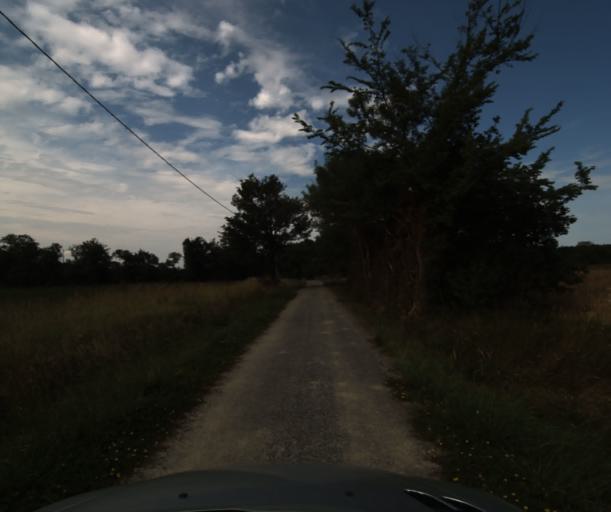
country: FR
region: Midi-Pyrenees
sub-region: Departement de la Haute-Garonne
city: Labastidette
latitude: 43.4904
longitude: 1.2203
